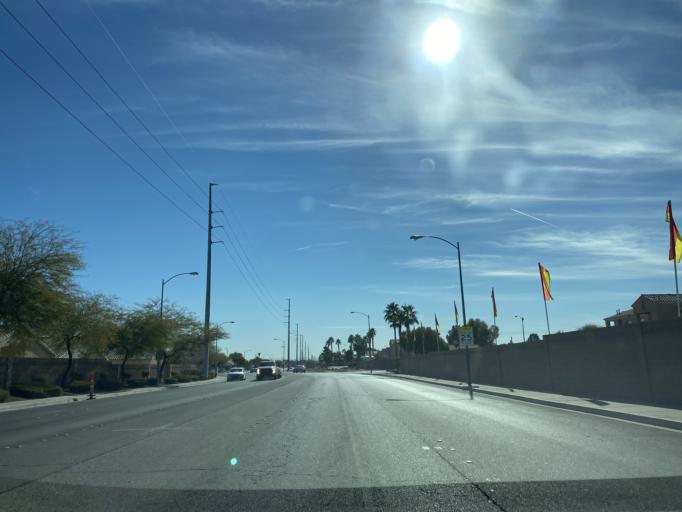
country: US
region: Nevada
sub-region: Clark County
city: North Las Vegas
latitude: 36.2489
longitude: -115.1441
